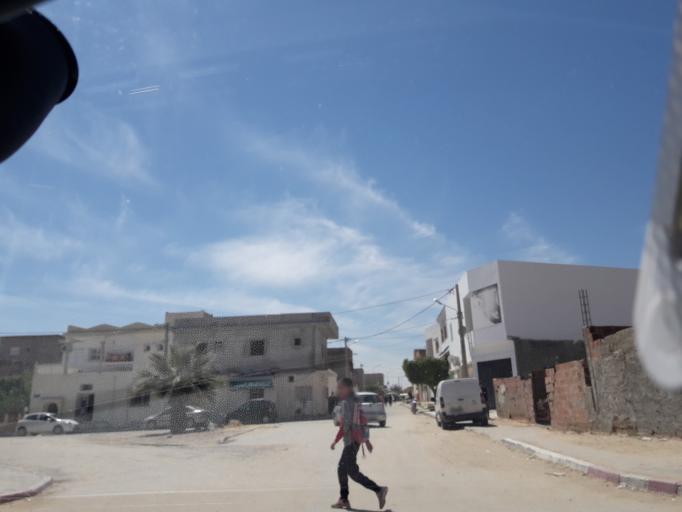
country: TN
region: Safaqis
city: Sfax
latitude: 34.7400
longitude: 10.5275
